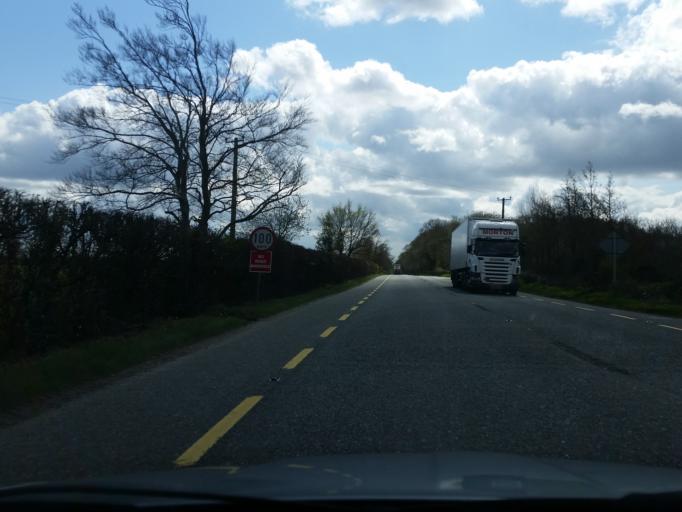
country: IE
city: Kentstown
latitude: 53.6359
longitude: -6.4951
